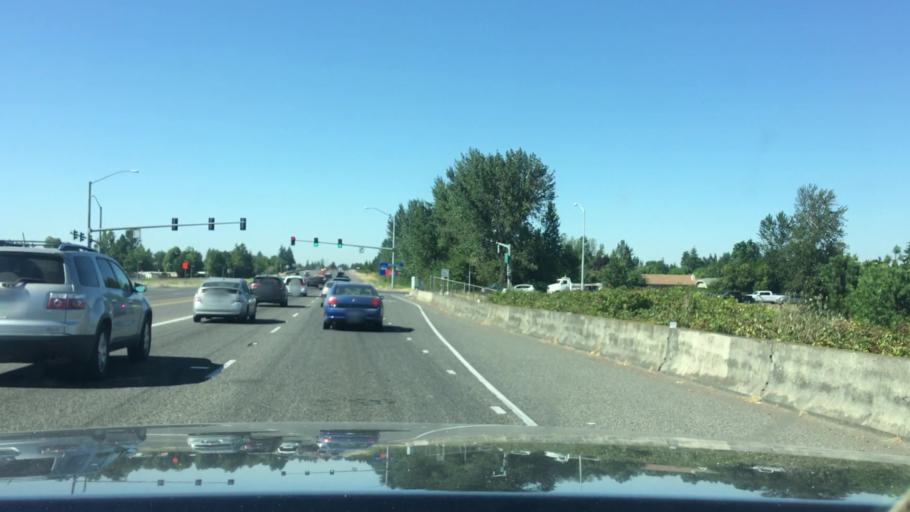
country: US
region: Oregon
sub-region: Lane County
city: Eugene
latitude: 44.0636
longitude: -123.1735
